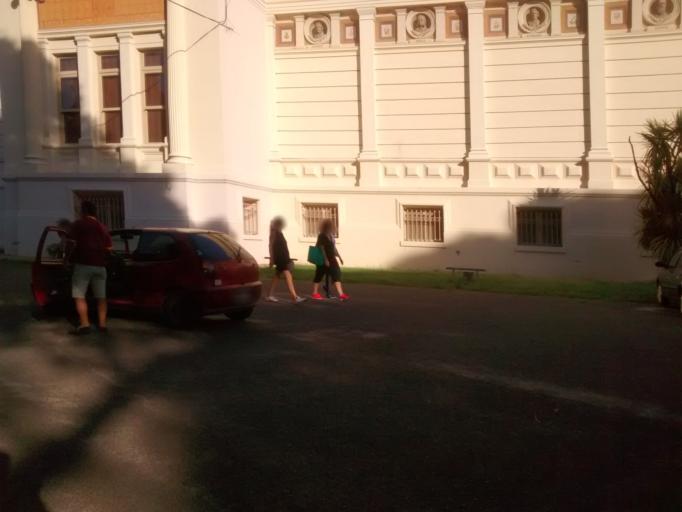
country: AR
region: Buenos Aires
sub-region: Partido de La Plata
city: La Plata
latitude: -34.9086
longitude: -57.9356
